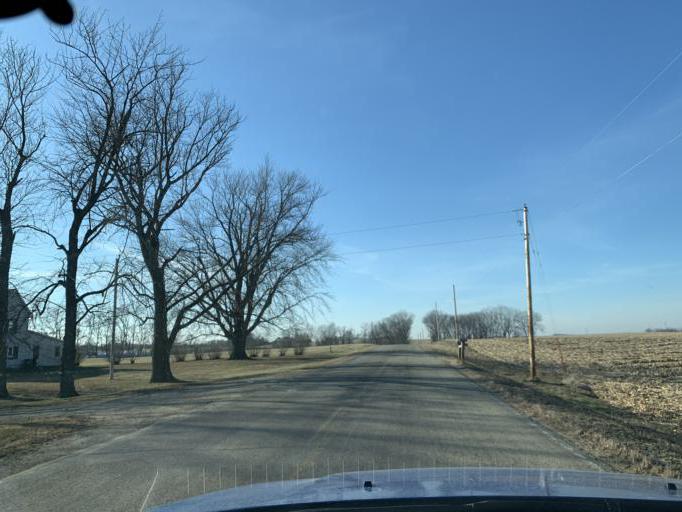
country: US
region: Wisconsin
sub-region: Iowa County
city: Barneveld
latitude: 42.8207
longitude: -89.9267
